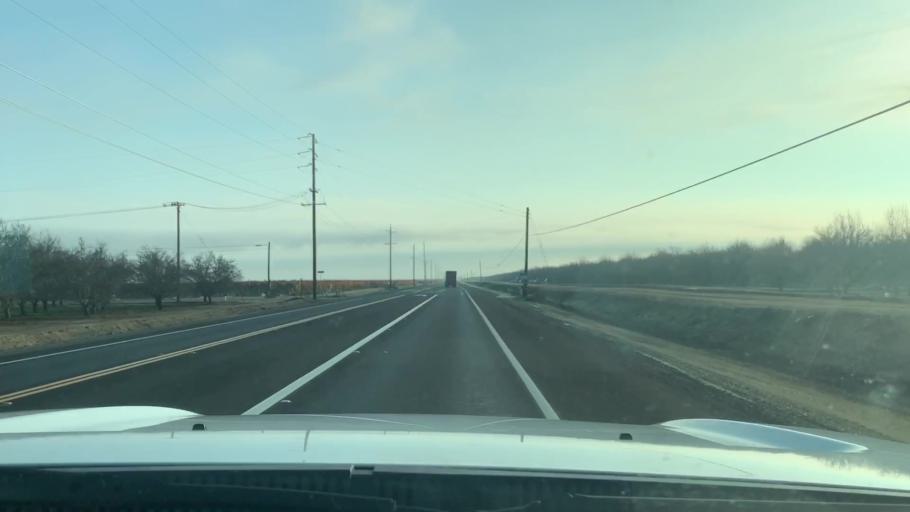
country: US
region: California
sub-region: Kern County
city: Wasco
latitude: 35.6017
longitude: -119.2779
